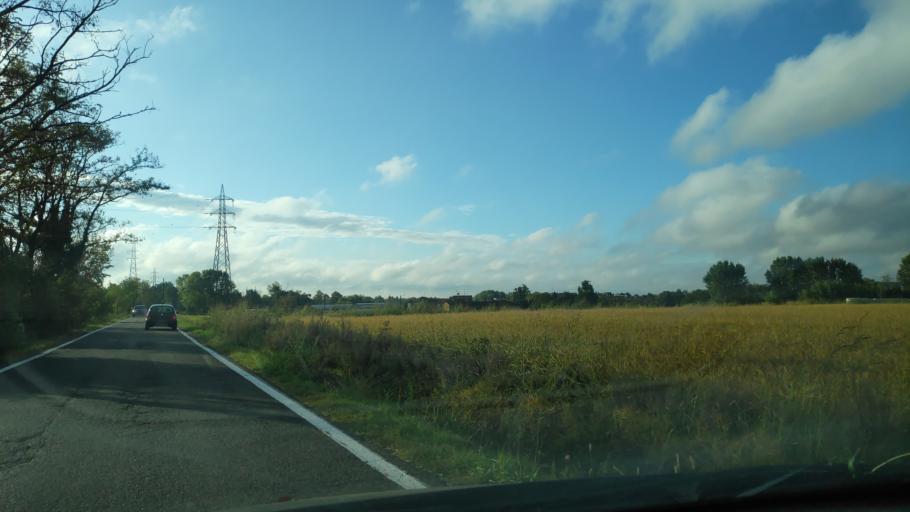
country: IT
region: Lombardy
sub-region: Citta metropolitana di Milano
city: Fizzonasco
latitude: 45.3806
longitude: 9.1919
